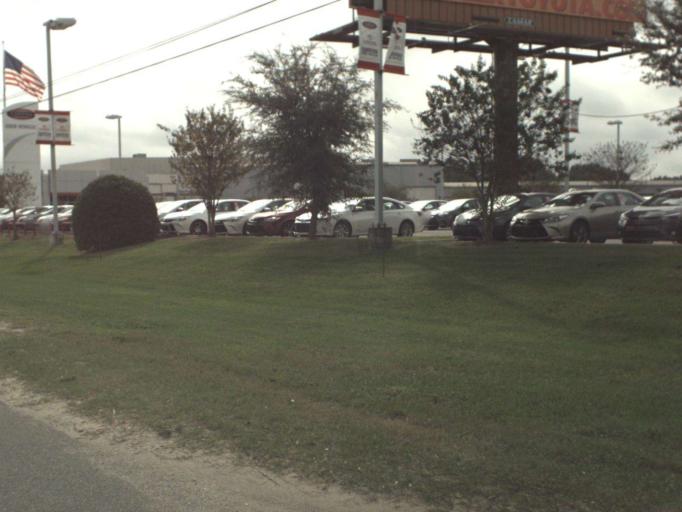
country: US
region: Florida
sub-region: Escambia County
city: Ensley
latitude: 30.4973
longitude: -87.2637
